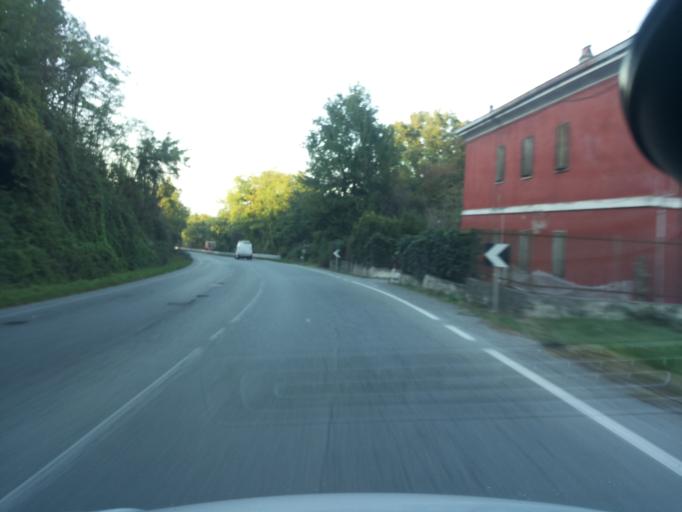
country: IT
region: Piedmont
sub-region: Provincia di Biella
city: Dorzano
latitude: 45.4293
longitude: 8.1118
